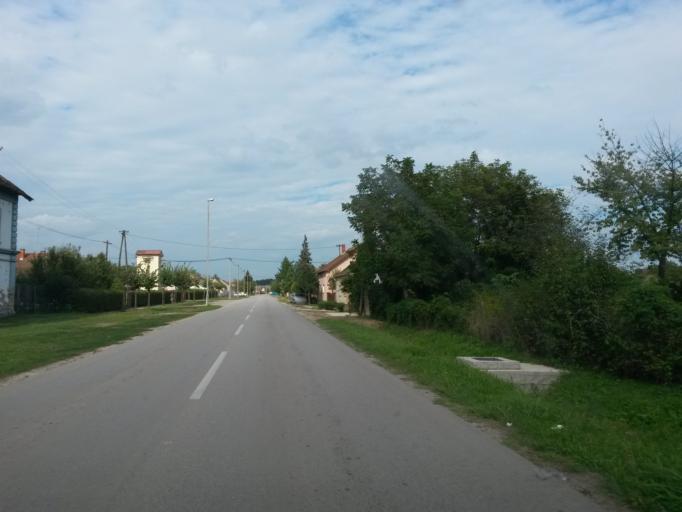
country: HR
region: Vukovarsko-Srijemska
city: Cerna
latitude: 45.1965
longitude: 18.6913
